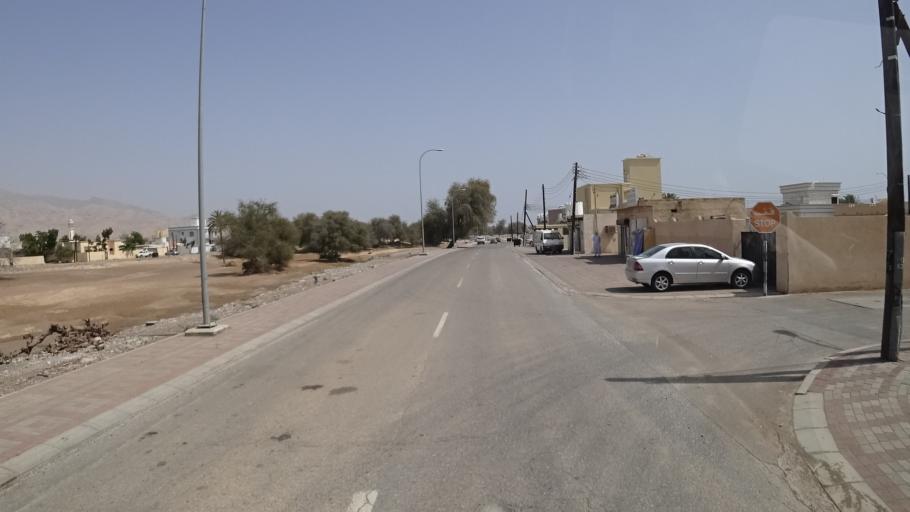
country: OM
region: Muhafazat Masqat
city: Muscat
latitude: 23.2401
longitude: 58.9110
